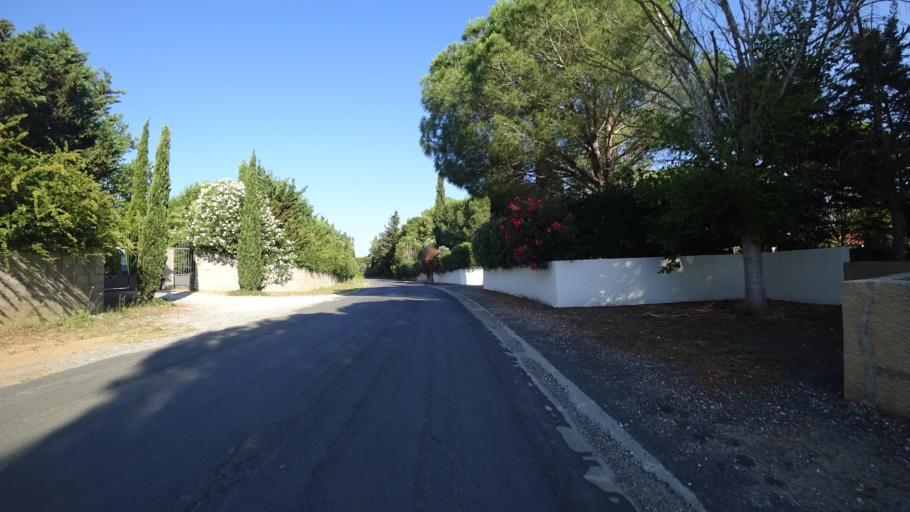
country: FR
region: Languedoc-Roussillon
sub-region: Departement des Pyrenees-Orientales
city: Villelongue-de-la-Salanque
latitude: 42.6949
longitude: 2.9722
